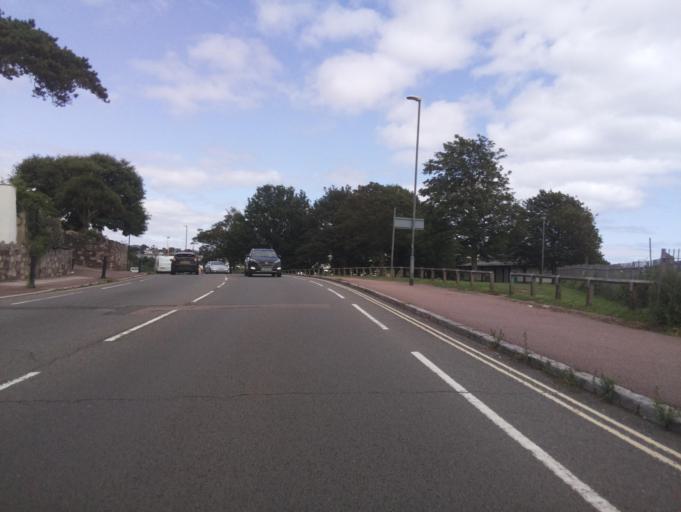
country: GB
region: England
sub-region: Borough of Torbay
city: Torquay
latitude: 50.4579
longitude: -3.5424
